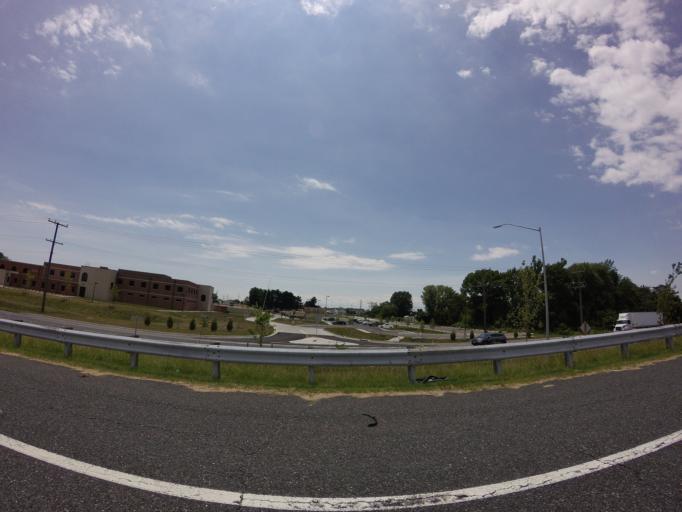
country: US
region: Maryland
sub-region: Baltimore County
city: Essex
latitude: 39.2876
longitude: -76.4994
